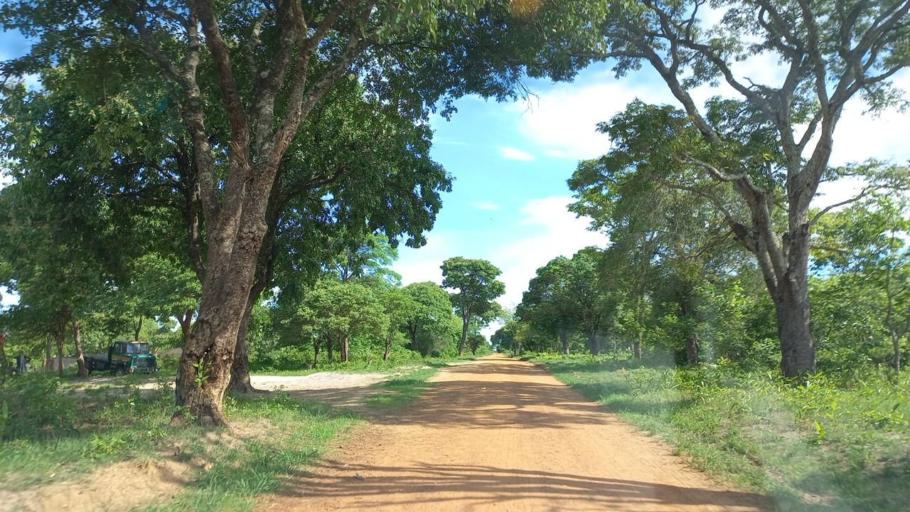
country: ZM
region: North-Western
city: Kabompo
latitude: -13.0691
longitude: 24.2183
